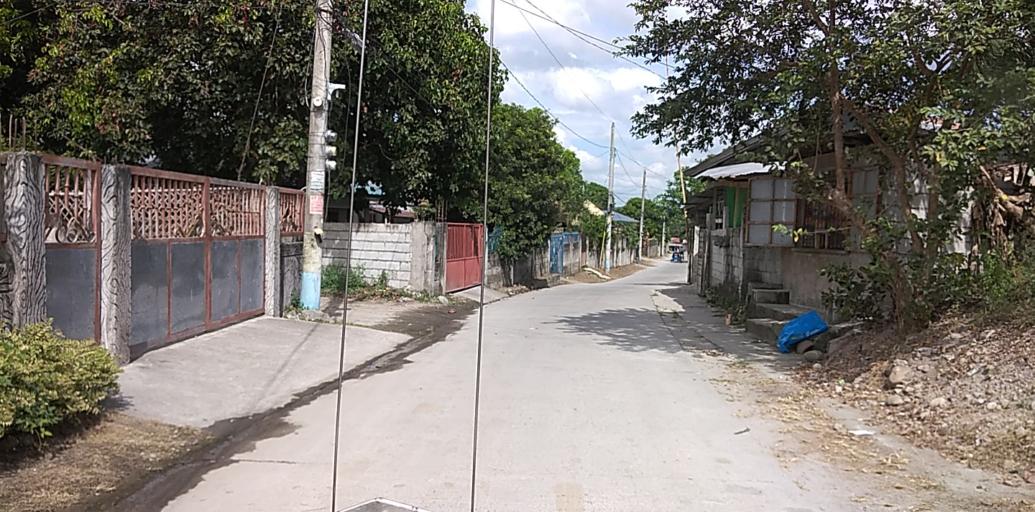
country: PH
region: Central Luzon
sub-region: Province of Pampanga
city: Porac
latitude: 15.0631
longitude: 120.5361
